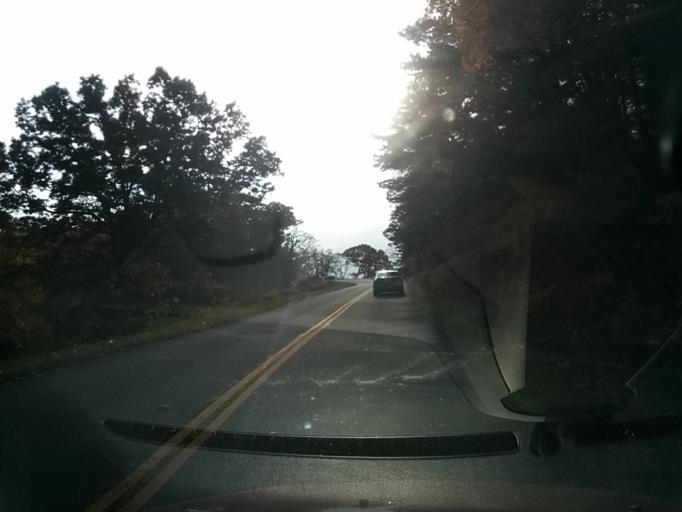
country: US
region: Virginia
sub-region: City of Buena Vista
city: Buena Vista
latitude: 37.7884
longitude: -79.2693
